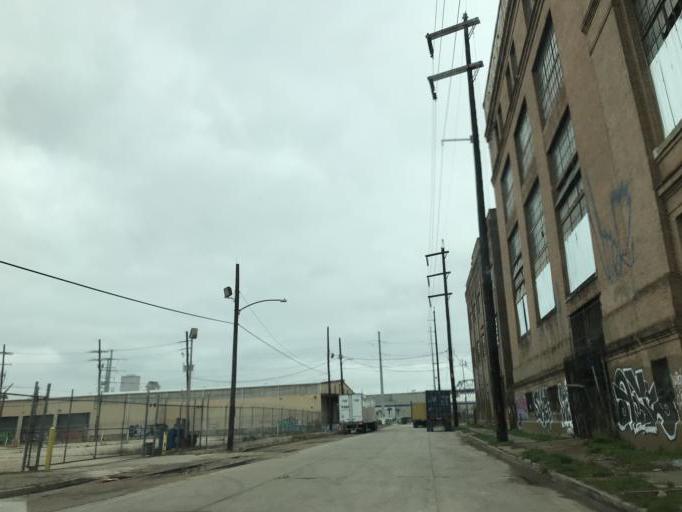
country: US
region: Louisiana
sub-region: Jefferson Parish
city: Gretna
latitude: 29.9299
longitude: -90.0650
